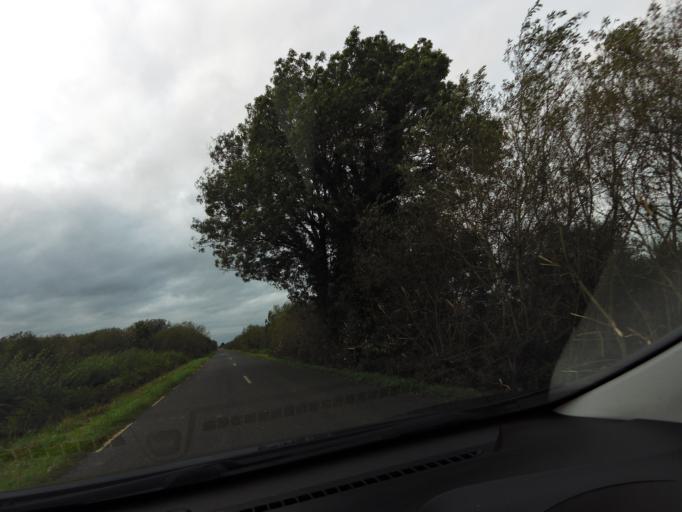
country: IE
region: Leinster
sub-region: Uibh Fhaili
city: Ferbane
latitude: 53.2044
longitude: -7.7842
